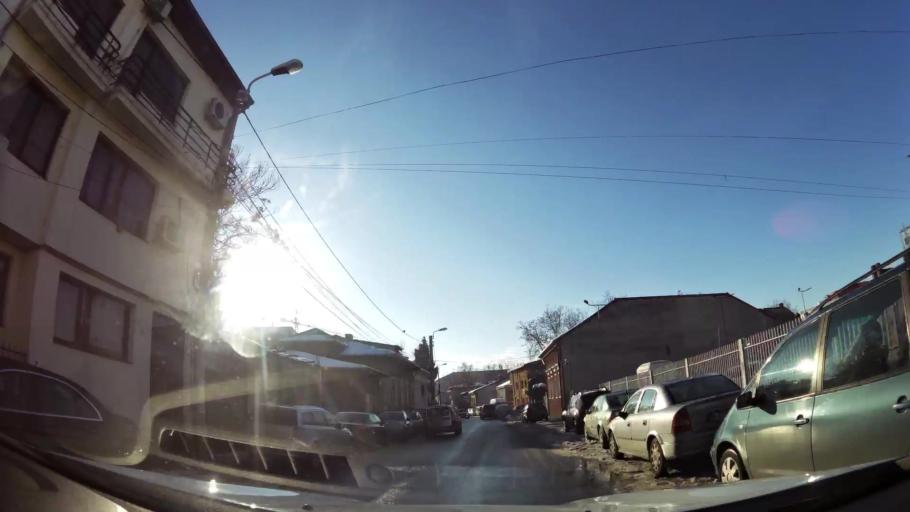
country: RO
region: Bucuresti
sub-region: Municipiul Bucuresti
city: Bucuresti
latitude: 44.4195
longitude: 26.1000
